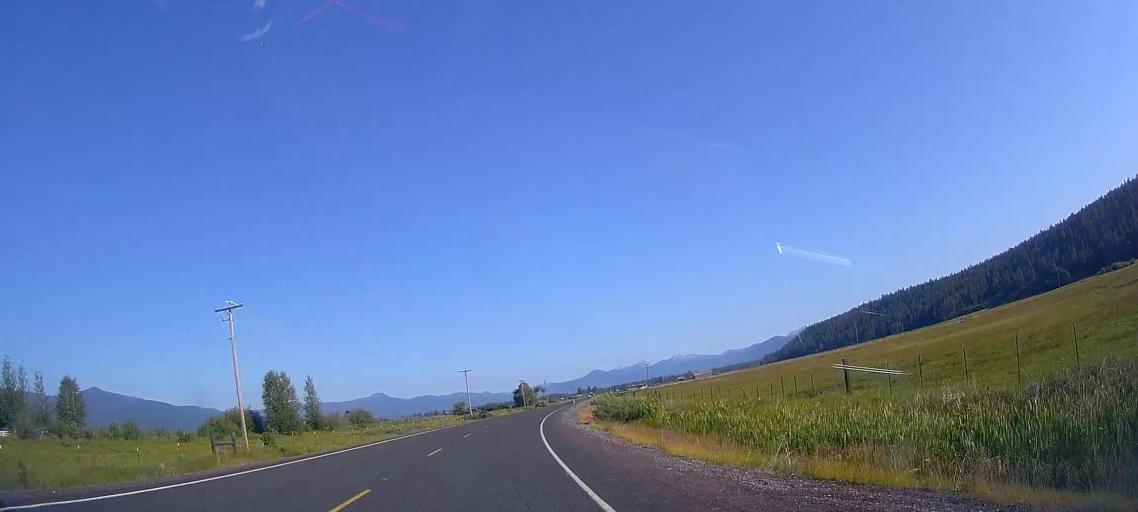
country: US
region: Oregon
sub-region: Klamath County
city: Klamath Falls
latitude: 42.6480
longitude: -121.9540
